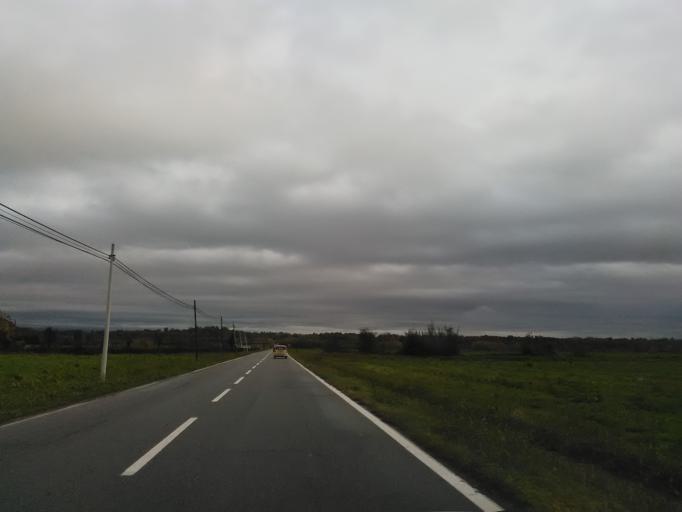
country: IT
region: Piedmont
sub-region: Provincia di Vercelli
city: Santhia
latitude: 45.3897
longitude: 8.1838
